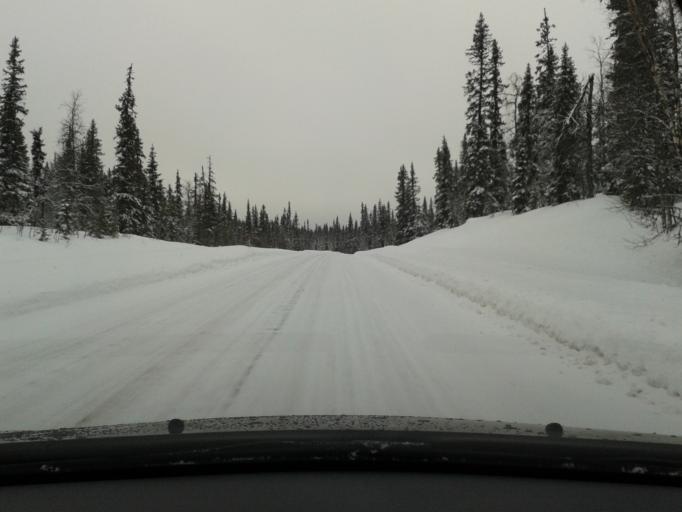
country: SE
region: Vaesterbotten
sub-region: Vilhelmina Kommun
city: Sjoberg
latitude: 65.1228
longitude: 15.8759
